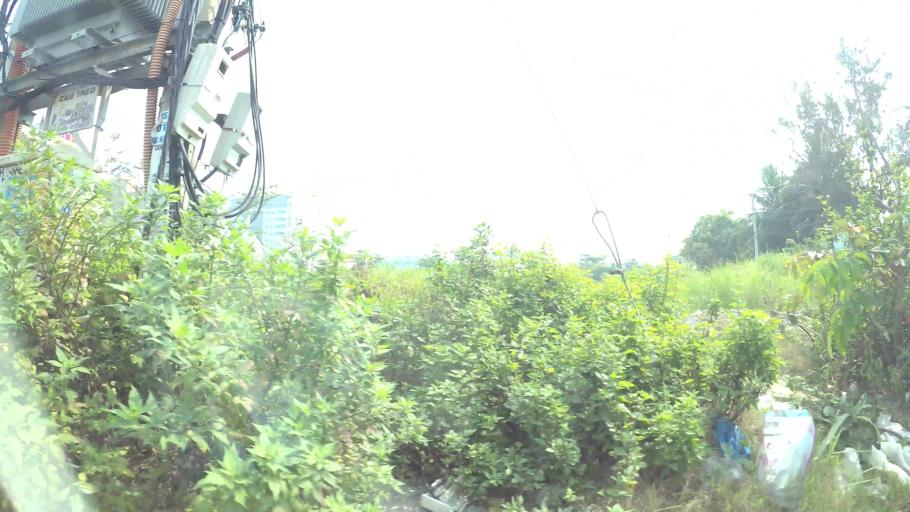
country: VN
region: Da Nang
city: Son Tra
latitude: 16.0449
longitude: 108.2473
